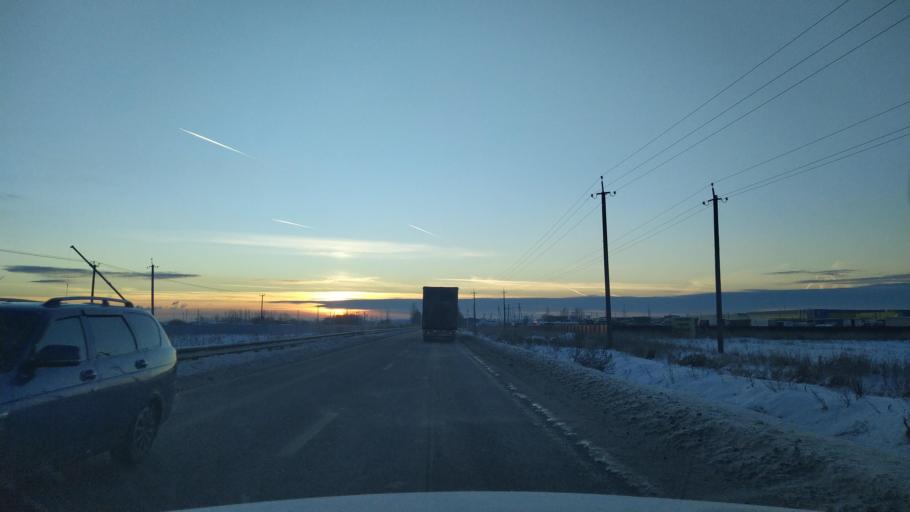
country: RU
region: St.-Petersburg
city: Petro-Slavyanka
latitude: 59.7784
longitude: 30.4766
